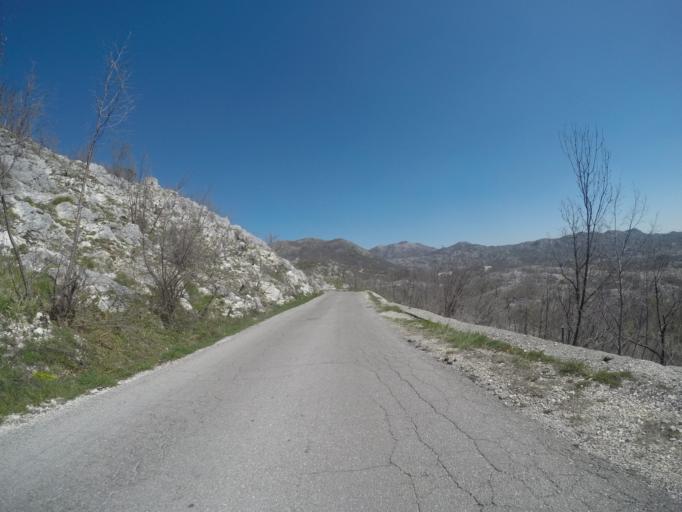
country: ME
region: Cetinje
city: Cetinje
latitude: 42.4389
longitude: 18.8716
